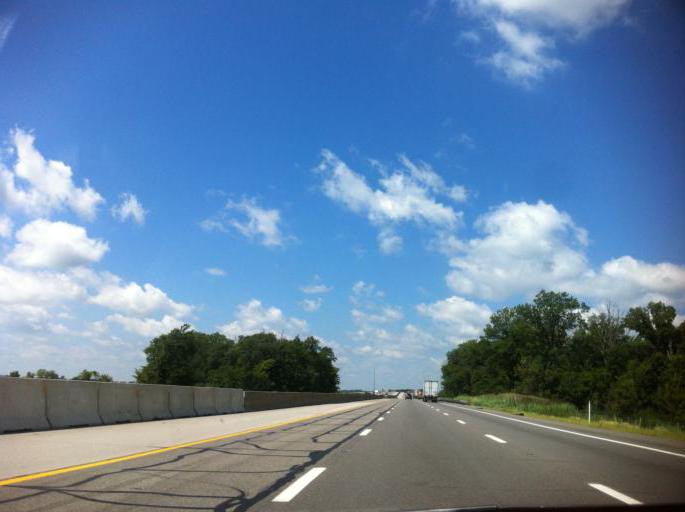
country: US
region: Ohio
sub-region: Sandusky County
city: Fremont
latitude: 41.3843
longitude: -83.0324
